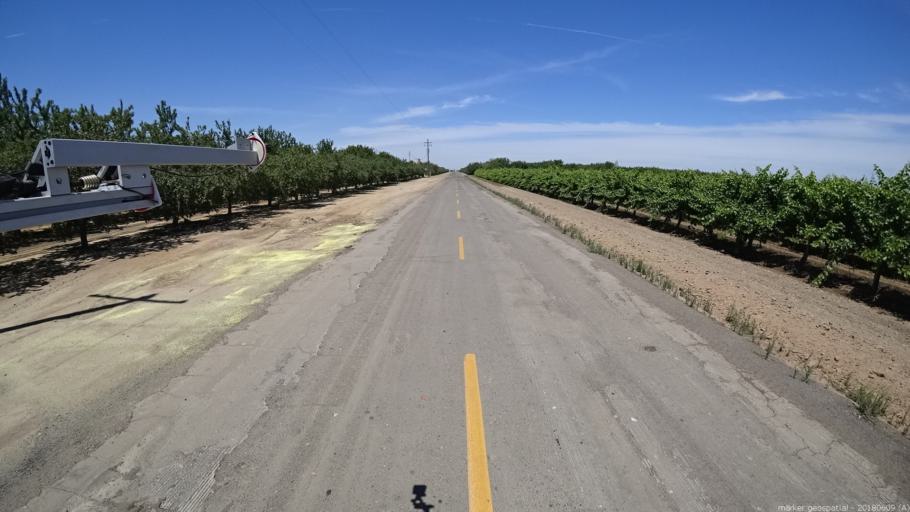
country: US
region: California
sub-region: Madera County
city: Madera
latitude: 36.9382
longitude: -120.1863
